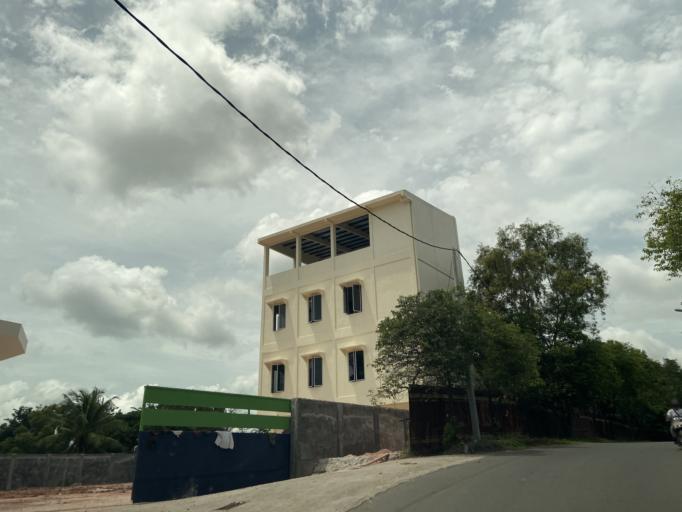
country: SG
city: Singapore
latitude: 1.1611
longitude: 104.0111
